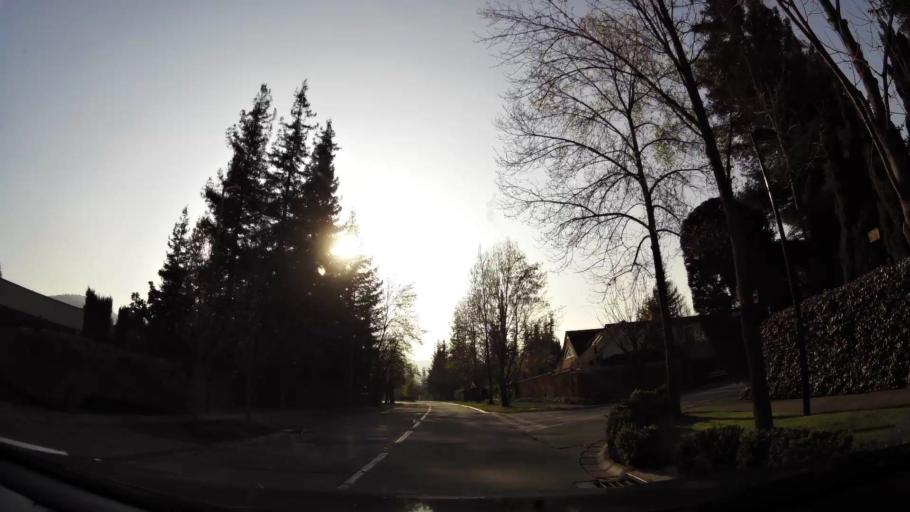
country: CL
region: Santiago Metropolitan
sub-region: Provincia de Santiago
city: Villa Presidente Frei, Nunoa, Santiago, Chile
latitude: -33.3512
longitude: -70.5355
